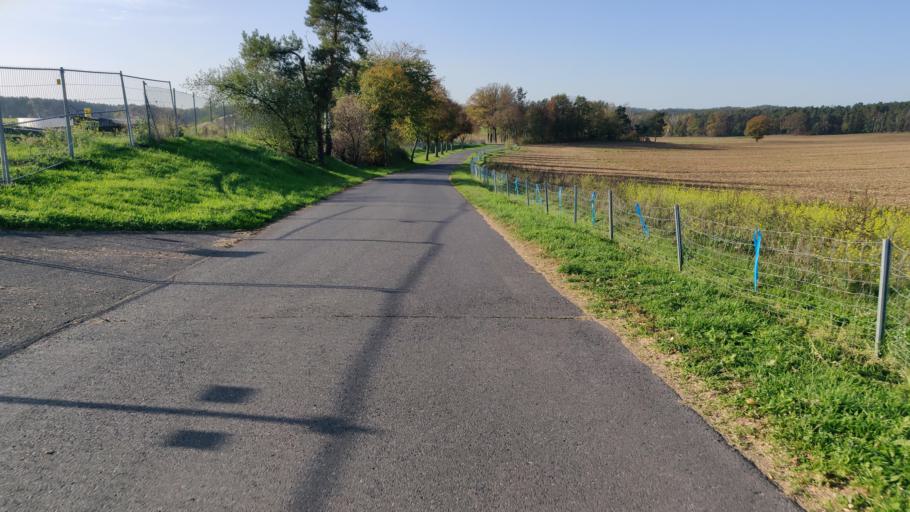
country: DE
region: Brandenburg
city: Ortrand
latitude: 51.3449
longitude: 13.7632
